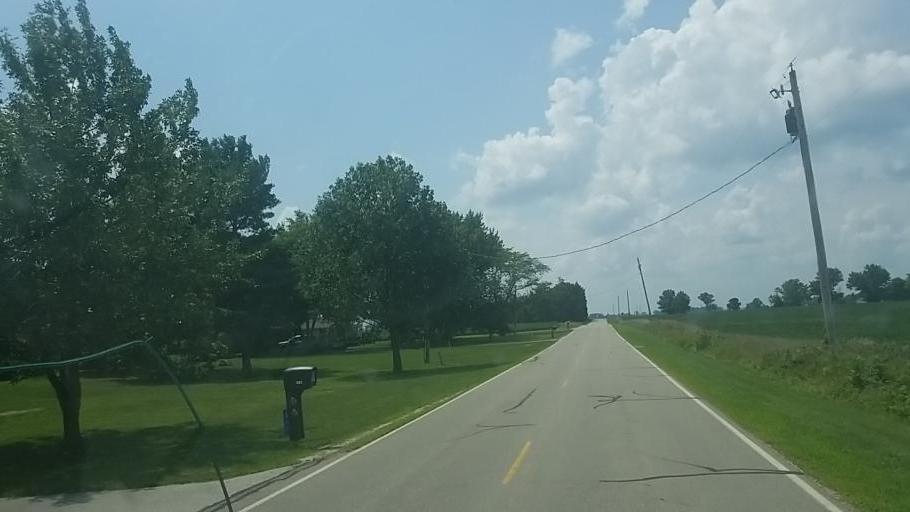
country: US
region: Ohio
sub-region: Crawford County
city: Bucyrus
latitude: 40.7511
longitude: -83.0696
